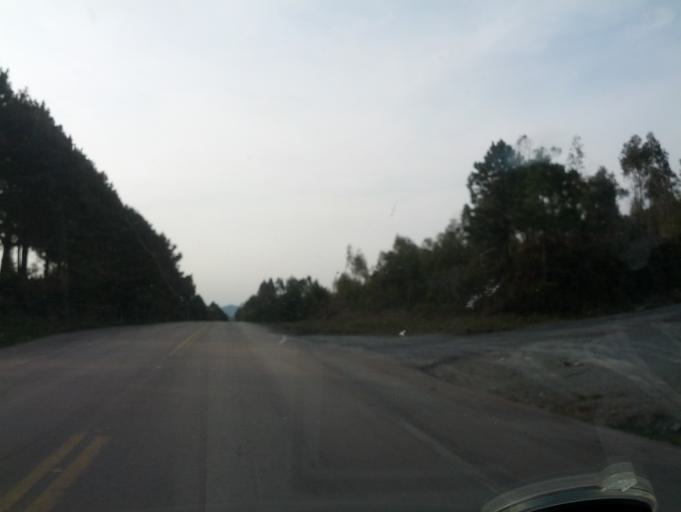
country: BR
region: Santa Catarina
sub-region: Otacilio Costa
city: Otacilio Costa
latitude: -27.3366
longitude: -50.1320
